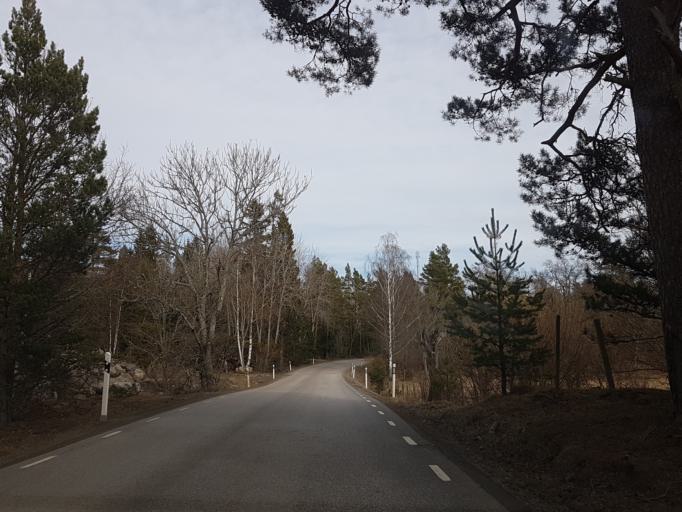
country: SE
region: Stockholm
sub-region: Norrtalje Kommun
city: Bjorko
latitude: 59.6674
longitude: 18.8702
